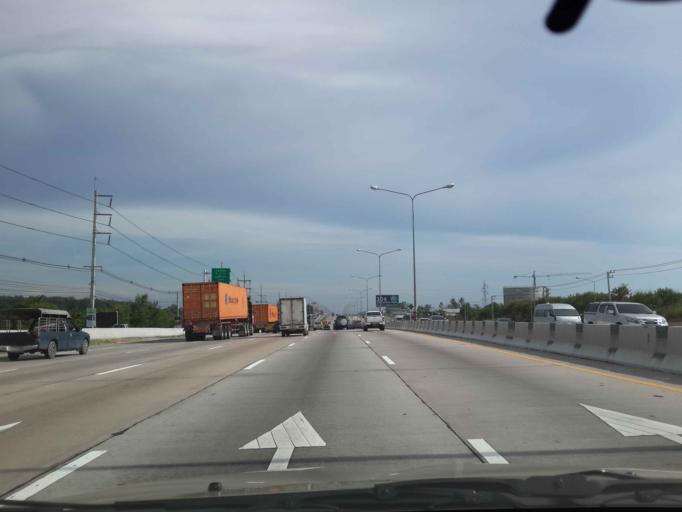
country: TH
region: Chon Buri
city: Si Racha
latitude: 13.1741
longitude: 100.9932
